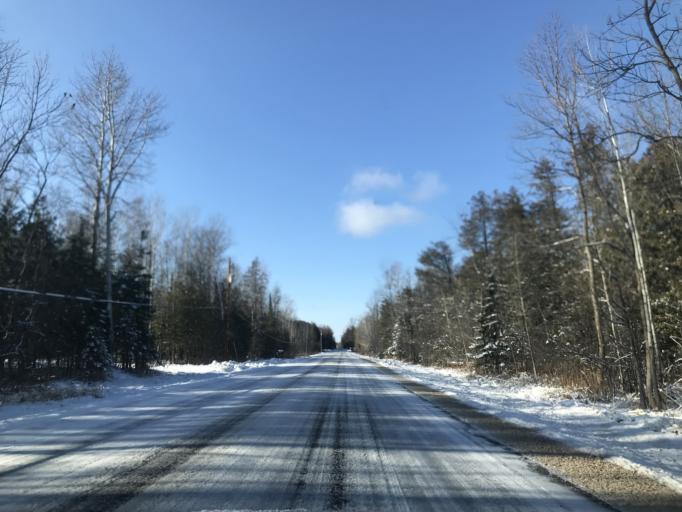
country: US
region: Wisconsin
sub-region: Door County
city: Sturgeon Bay
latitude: 44.8495
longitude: -87.4938
